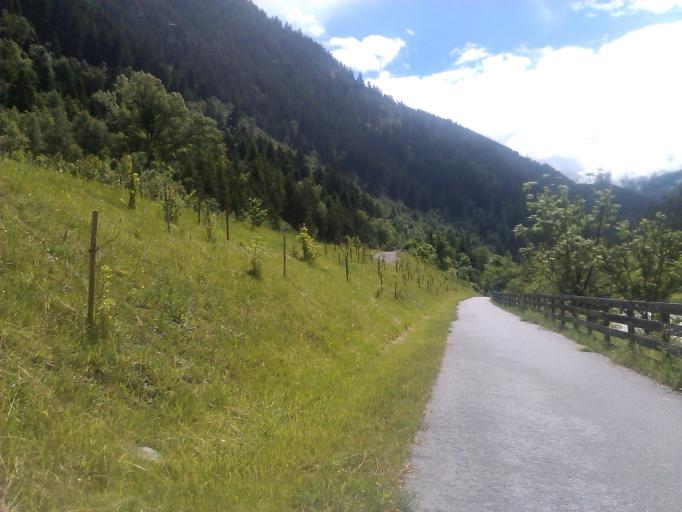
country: AT
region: Tyrol
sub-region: Politischer Bezirk Landeck
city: Prutz
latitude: 47.1132
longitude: 10.6539
